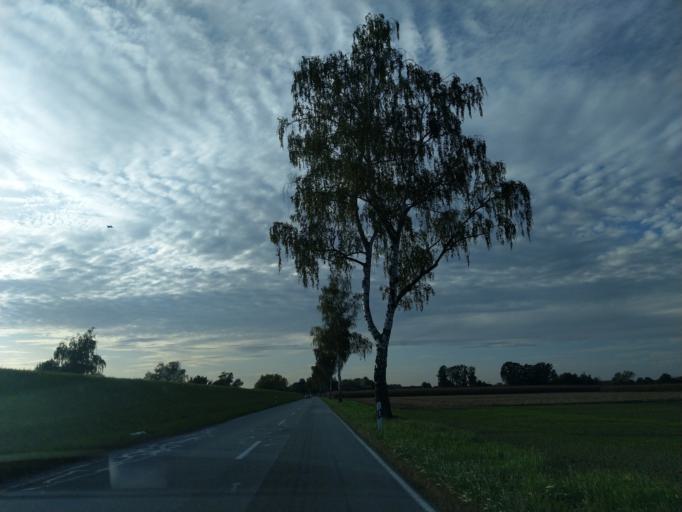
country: DE
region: Bavaria
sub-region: Lower Bavaria
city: Offenberg
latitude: 48.8434
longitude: 12.8695
